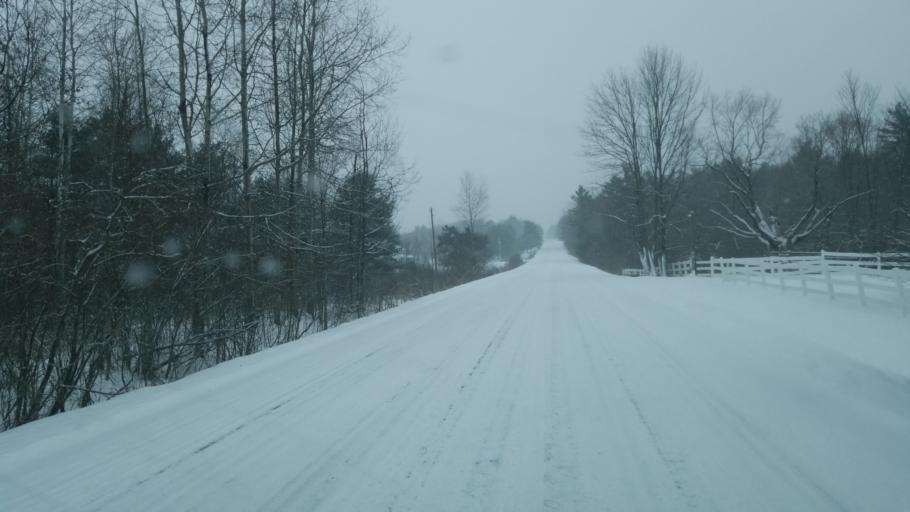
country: US
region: Michigan
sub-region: Mecosta County
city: Canadian Lakes
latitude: 43.5766
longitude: -85.4098
